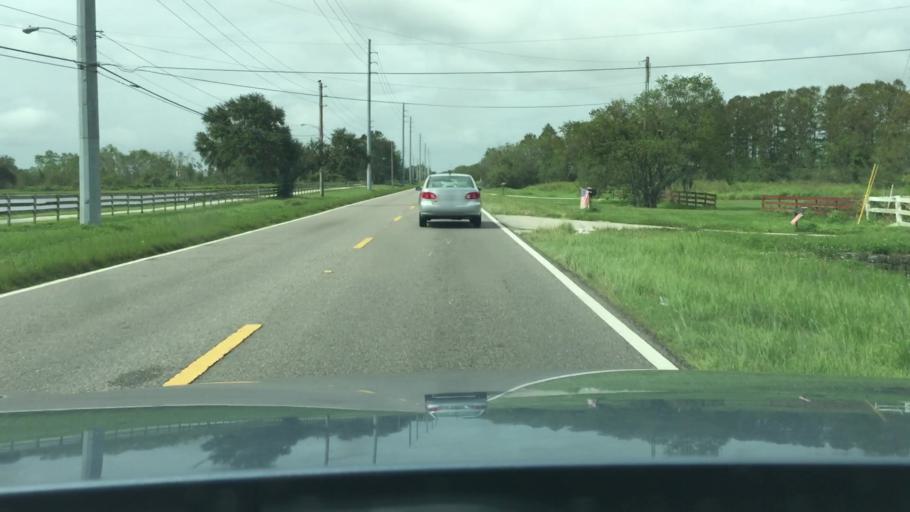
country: US
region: Florida
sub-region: Osceola County
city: Buenaventura Lakes
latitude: 28.2701
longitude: -81.3527
